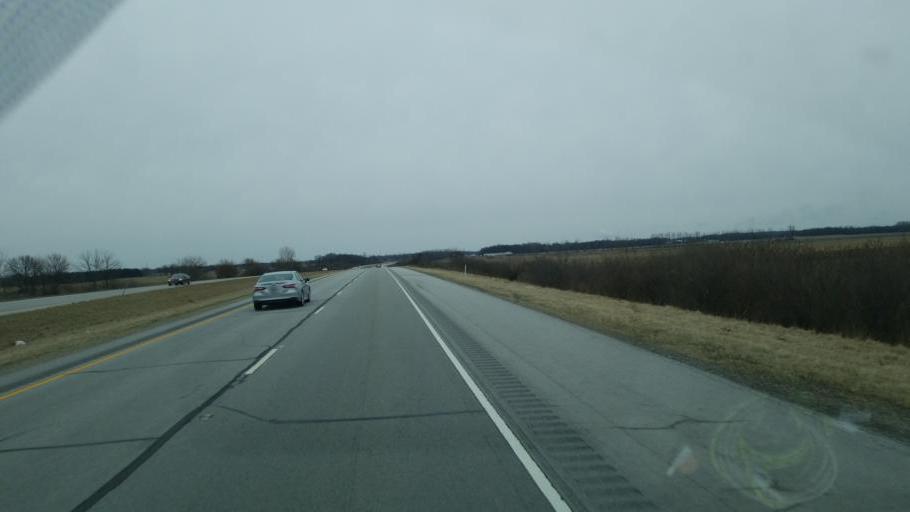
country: US
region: Indiana
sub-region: Marshall County
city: Argos
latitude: 41.2652
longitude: -86.2669
